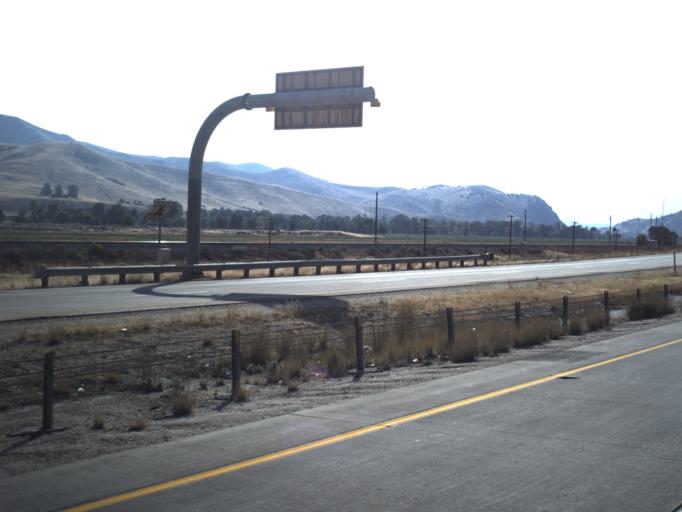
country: US
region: Utah
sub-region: Morgan County
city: Morgan
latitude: 41.0512
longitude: -111.6165
